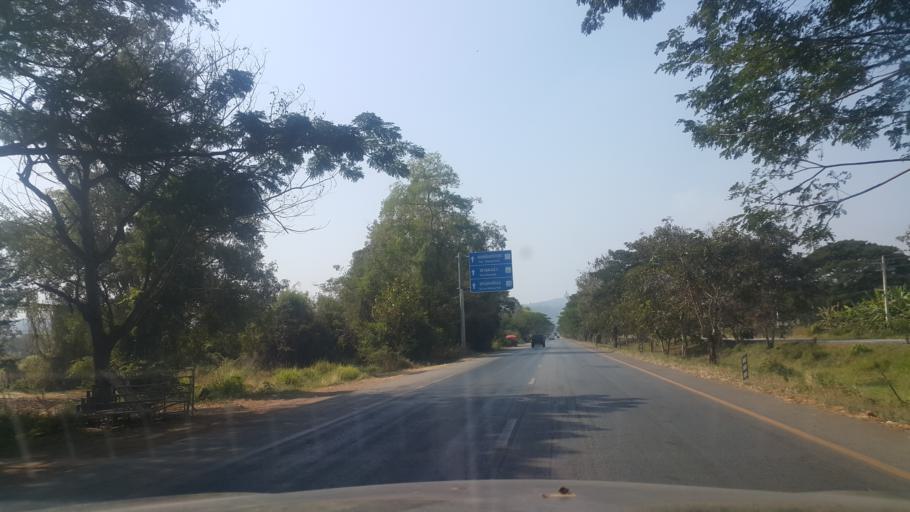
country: TH
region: Nakhon Ratchasima
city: Wang Nam Khiao
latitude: 14.5186
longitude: 101.9625
